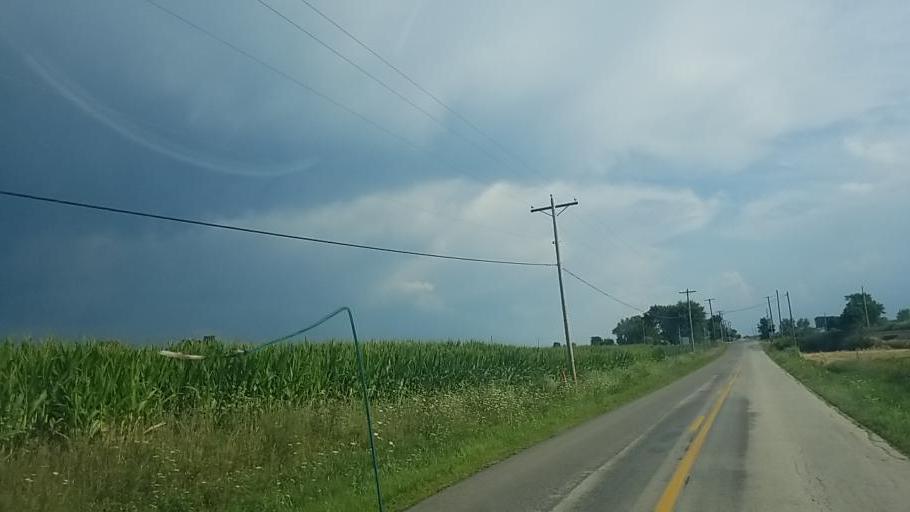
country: US
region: Ohio
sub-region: Wayne County
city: Smithville
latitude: 40.8905
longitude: -81.8611
